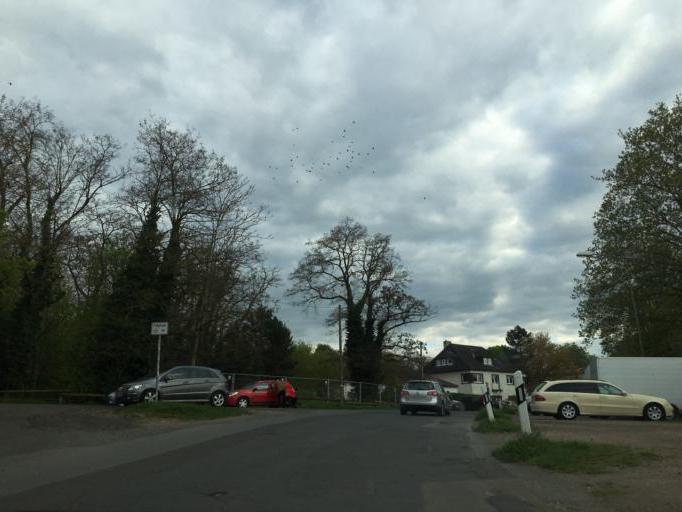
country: DE
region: Hesse
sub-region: Regierungsbezirk Darmstadt
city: Offenbach
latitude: 50.1011
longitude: 8.7943
